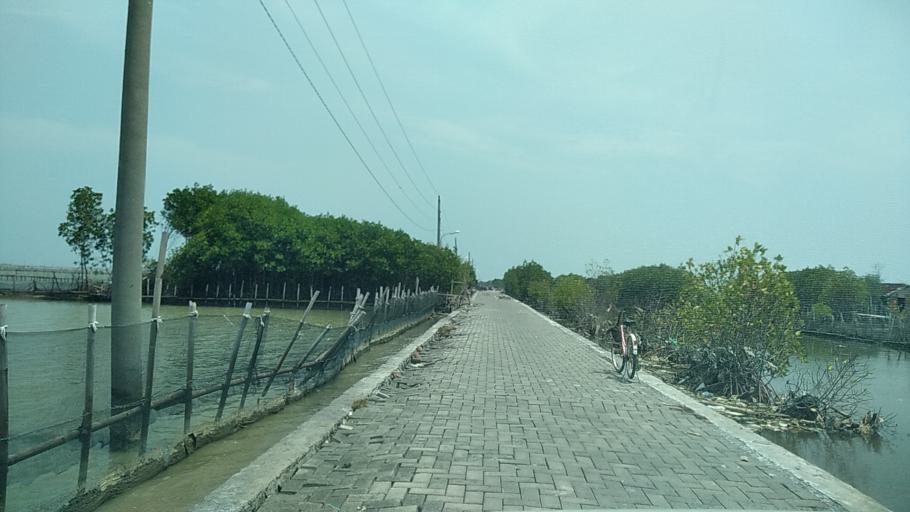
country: ID
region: Central Java
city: Semarang
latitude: -6.9458
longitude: 110.4415
